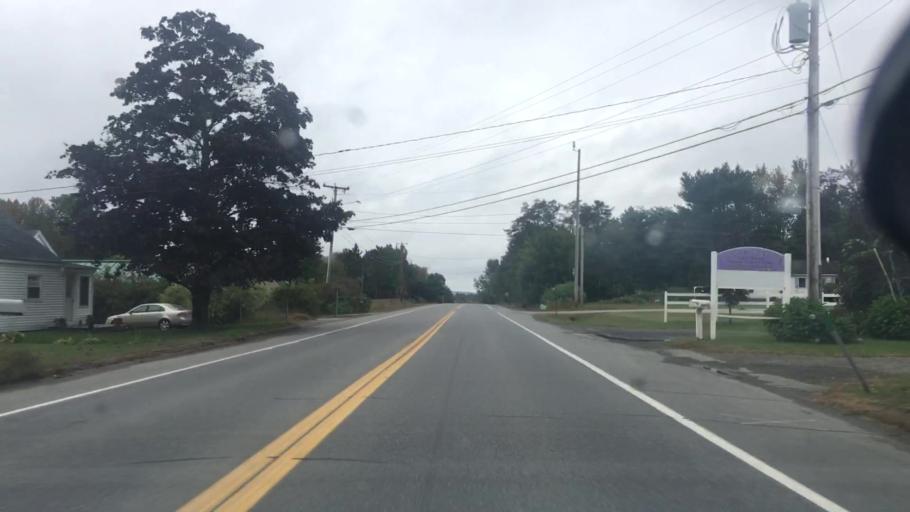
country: US
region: Maine
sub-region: Kennebec County
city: Belgrade
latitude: 44.3927
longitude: -69.8027
